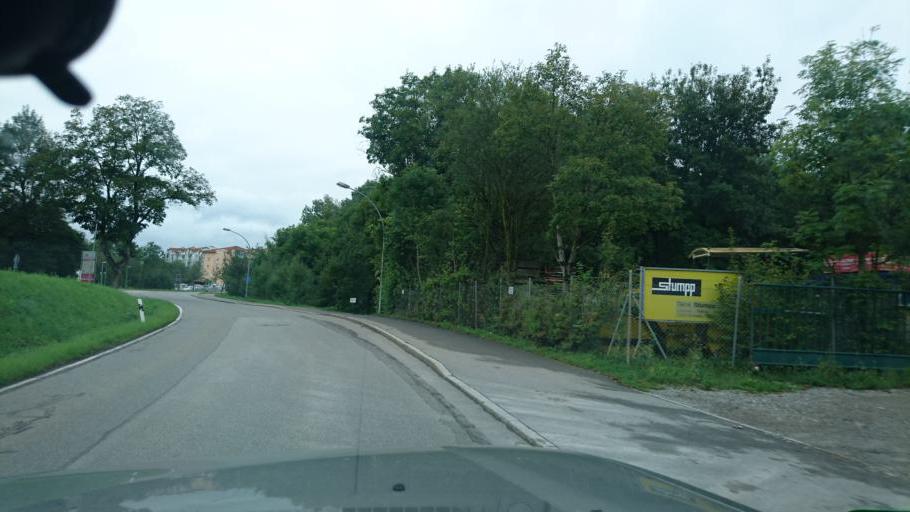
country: DE
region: Baden-Wuerttemberg
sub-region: Freiburg Region
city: Rottweil
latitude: 48.1736
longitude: 8.6137
